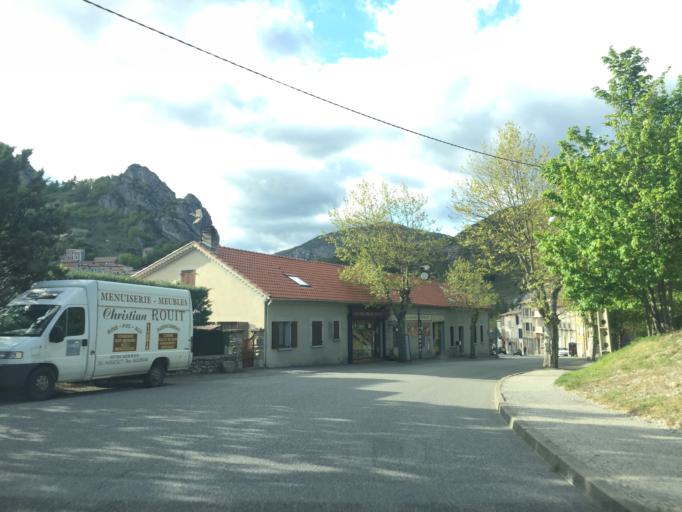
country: FR
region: Provence-Alpes-Cote d'Azur
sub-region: Departement des Hautes-Alpes
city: Serres
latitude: 44.4267
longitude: 5.7182
